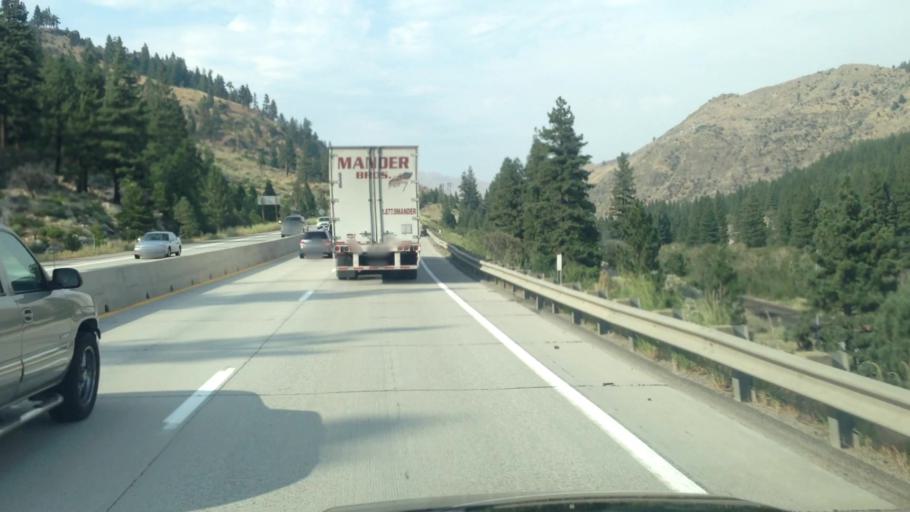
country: US
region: Nevada
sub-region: Washoe County
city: Verdi
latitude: 39.4613
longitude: -120.0073
